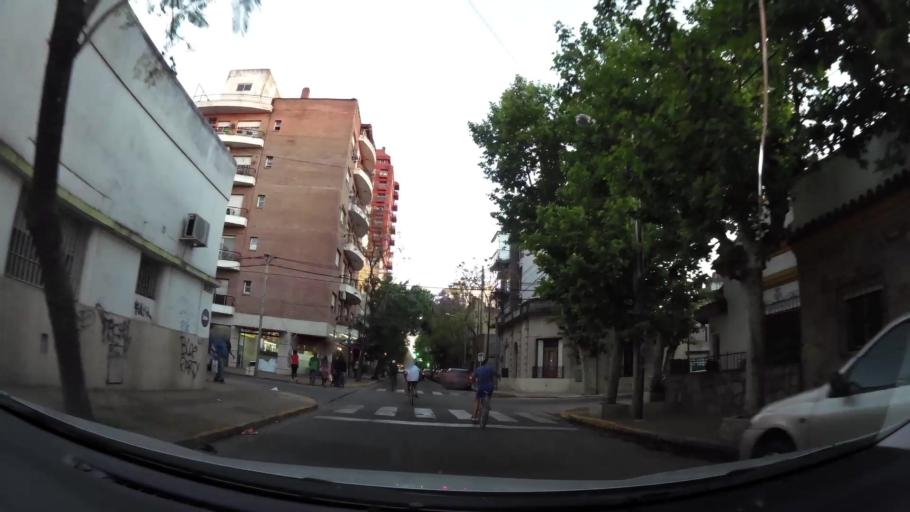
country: AR
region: Buenos Aires
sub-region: Partido de Tigre
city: Tigre
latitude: -34.4399
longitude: -58.5598
